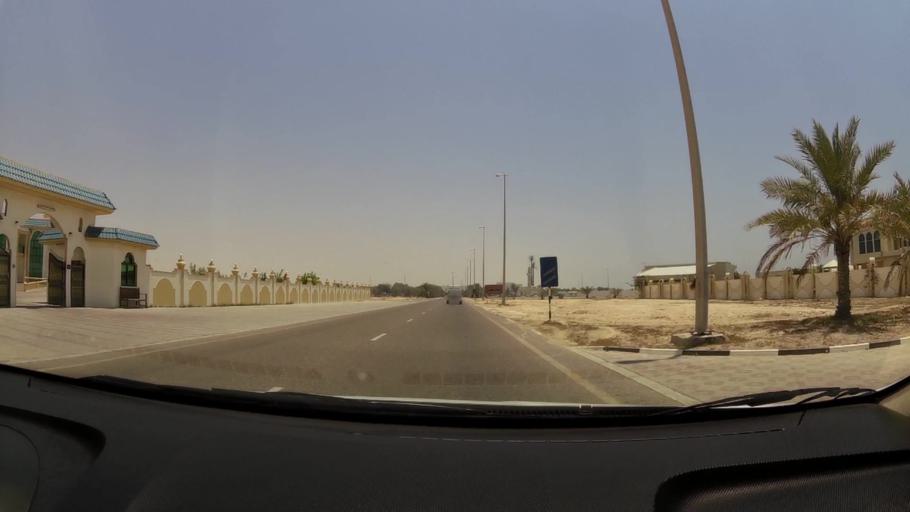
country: AE
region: Umm al Qaywayn
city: Umm al Qaywayn
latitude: 25.5337
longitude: 55.5323
